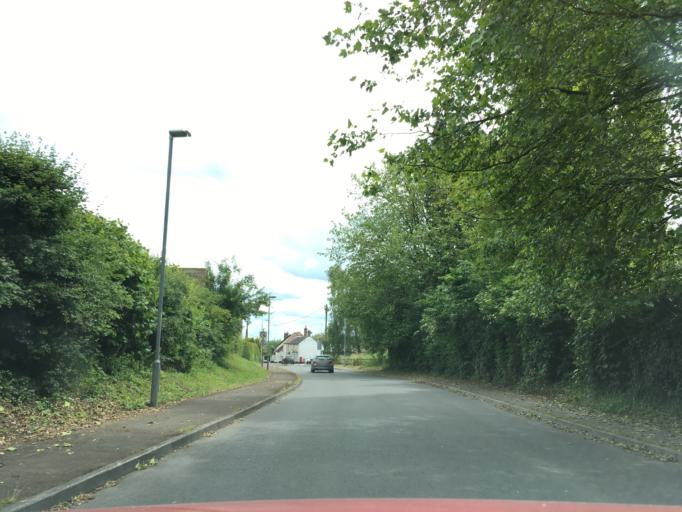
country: GB
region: England
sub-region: Wiltshire
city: Purton
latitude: 51.5721
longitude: -1.8649
